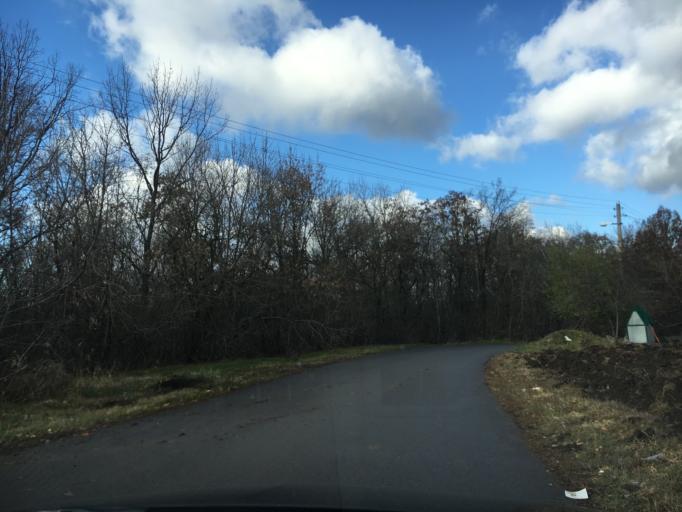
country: RU
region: Rostov
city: Pokrovskoye
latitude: 47.4825
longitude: 38.9134
